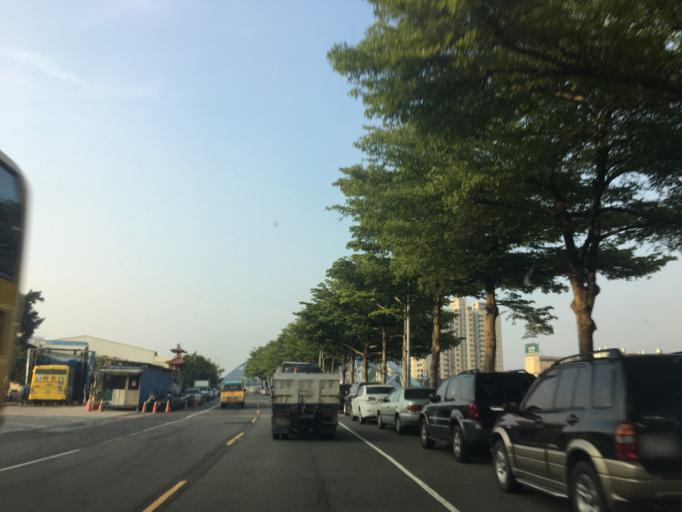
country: TW
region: Taiwan
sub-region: Taichung City
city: Taichung
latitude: 24.1569
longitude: 120.7037
